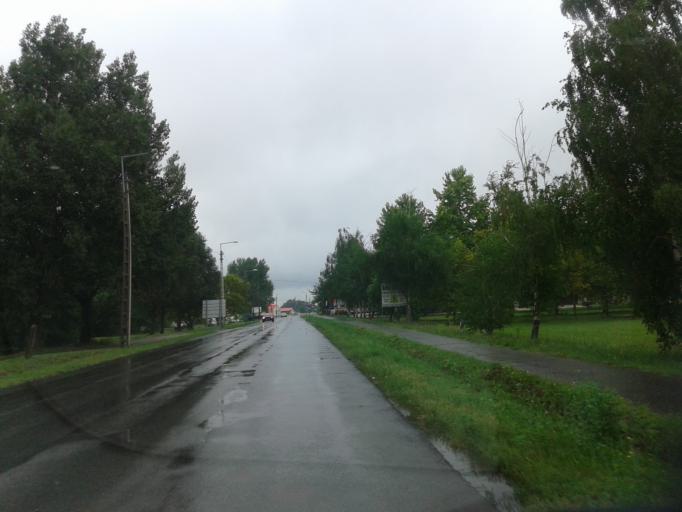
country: HU
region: Bacs-Kiskun
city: Kiskunhalas
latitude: 46.4558
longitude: 19.4665
